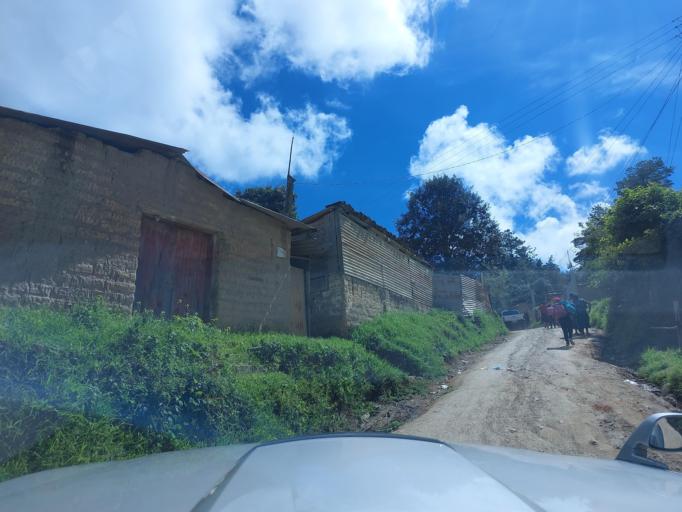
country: GT
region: Chimaltenango
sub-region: Municipio de San Juan Comalapa
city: Comalapa
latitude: 14.7543
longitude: -90.8899
